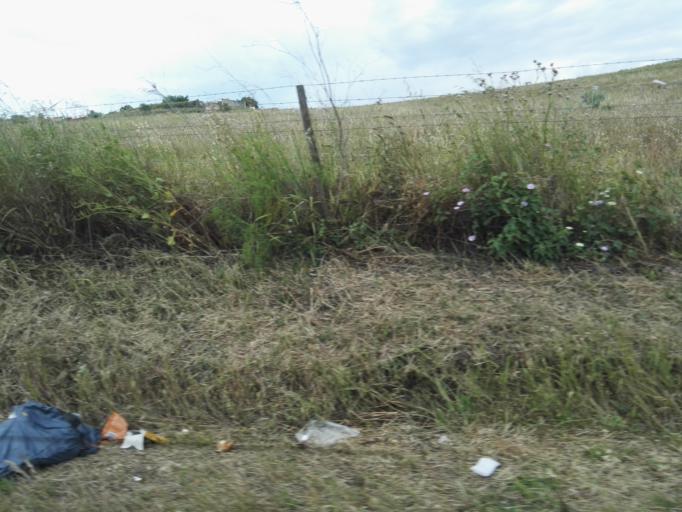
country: PT
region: Portalegre
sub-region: Elvas
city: Elvas
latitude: 38.8730
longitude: -7.1542
